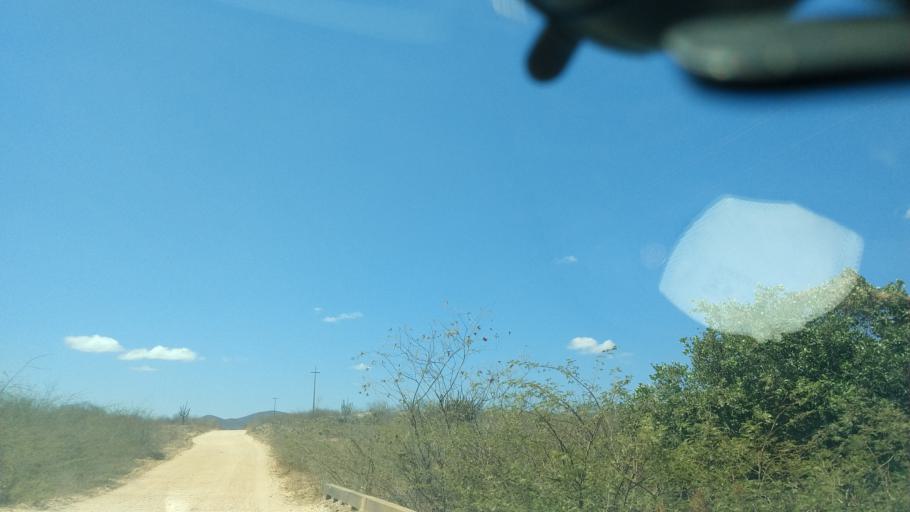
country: BR
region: Rio Grande do Norte
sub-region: Sao Tome
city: Sao Tome
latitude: -5.9771
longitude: -36.1711
